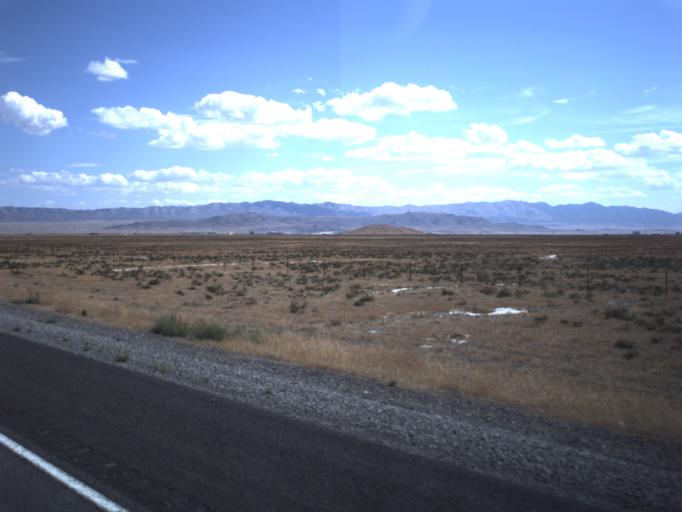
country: US
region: Utah
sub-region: Tooele County
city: Grantsville
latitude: 40.7255
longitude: -113.1792
